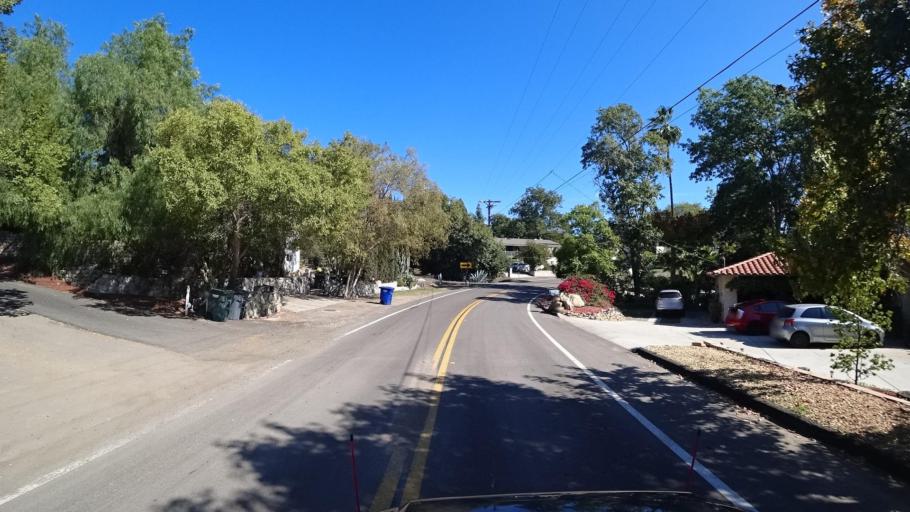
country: US
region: California
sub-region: San Diego County
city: Casa de Oro-Mount Helix
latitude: 32.7539
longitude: -116.9820
